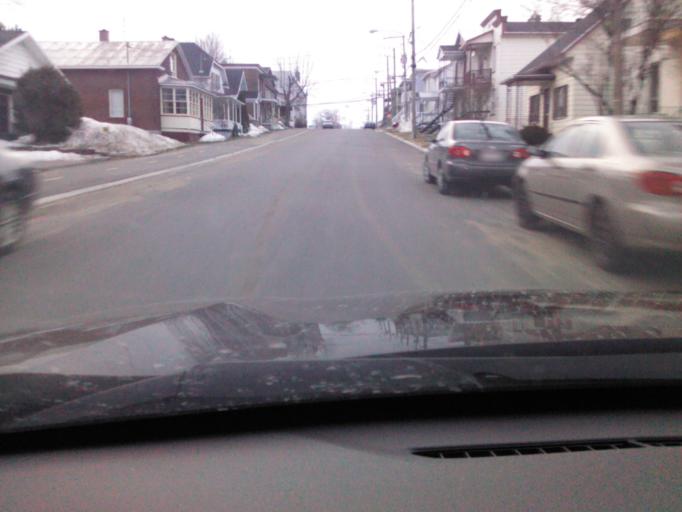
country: CA
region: Quebec
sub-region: Capitale-Nationale
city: Donnacona
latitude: 46.6738
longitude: -71.7370
